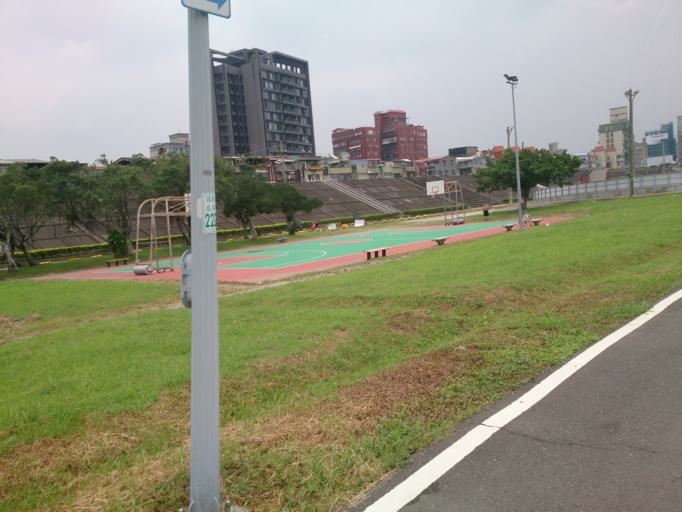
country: TW
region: Taipei
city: Taipei
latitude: 25.0845
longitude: 121.5135
